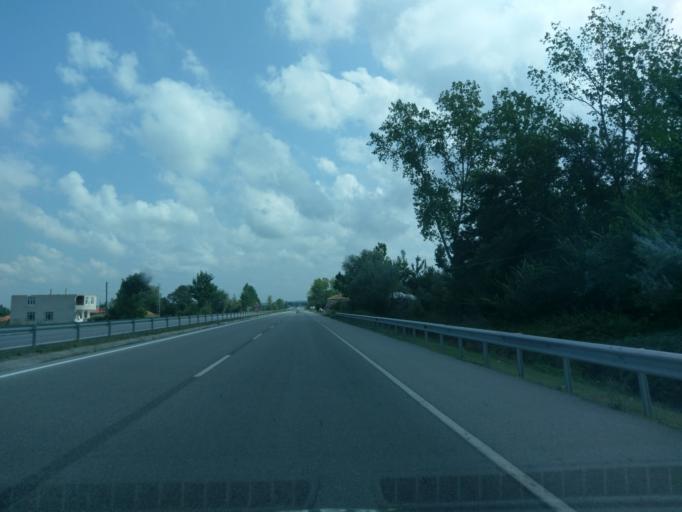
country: TR
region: Samsun
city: Alacam
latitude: 41.6101
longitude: 35.7194
